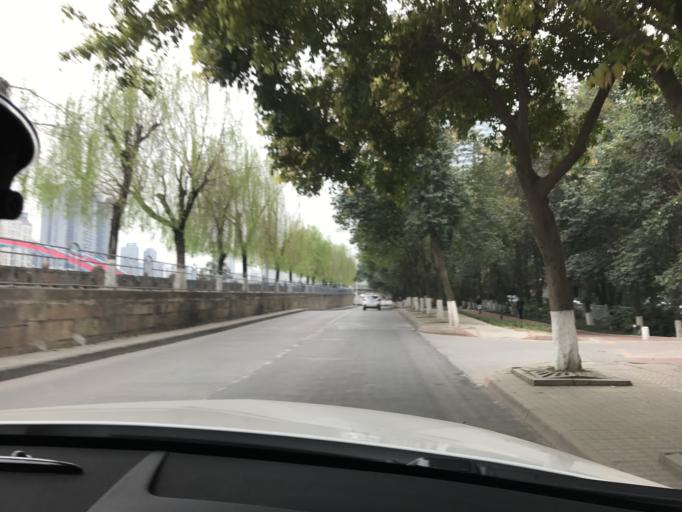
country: CN
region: Sichuan
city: Mianyang
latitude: 31.4533
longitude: 104.7471
